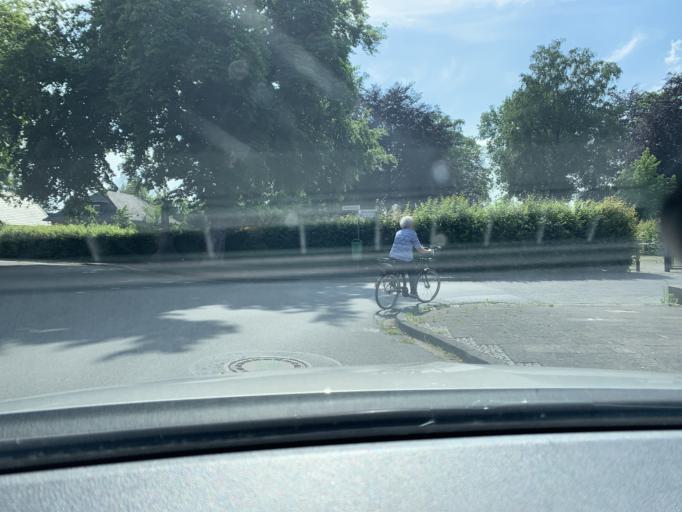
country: DE
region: North Rhine-Westphalia
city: Rietberg
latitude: 51.8031
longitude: 8.4240
